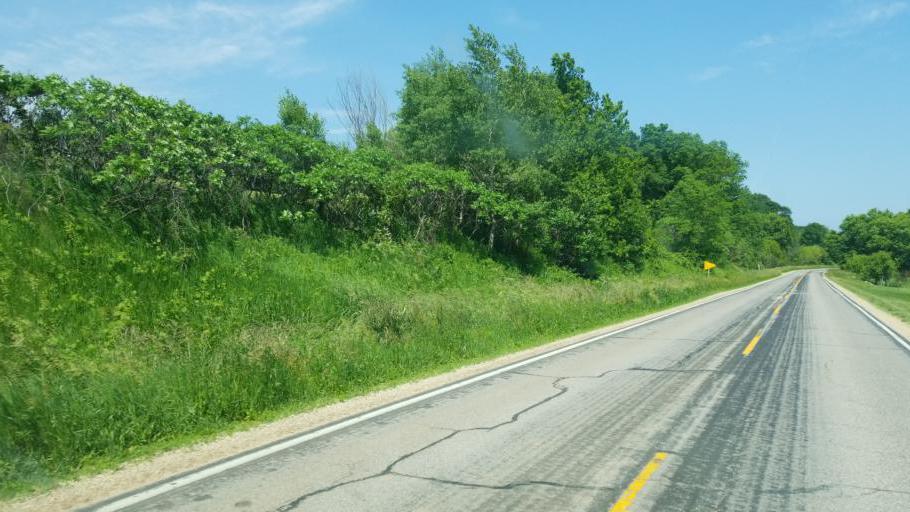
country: US
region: Wisconsin
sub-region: Vernon County
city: Hillsboro
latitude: 43.6451
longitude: -90.4241
